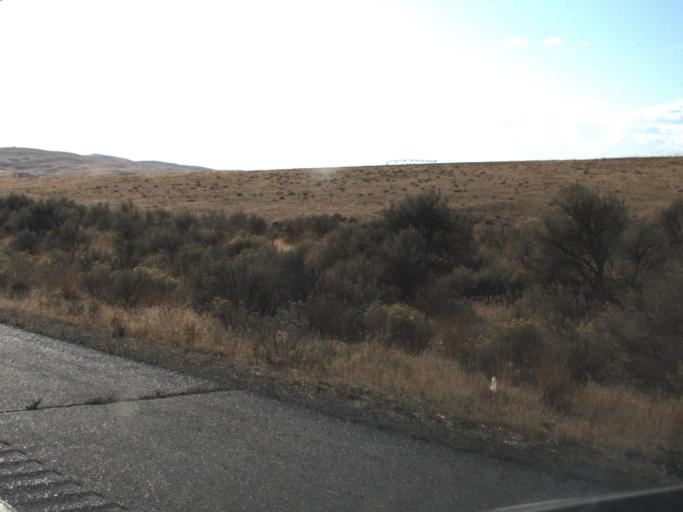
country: US
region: Oregon
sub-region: Umatilla County
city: Umatilla
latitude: 46.0164
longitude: -119.2279
